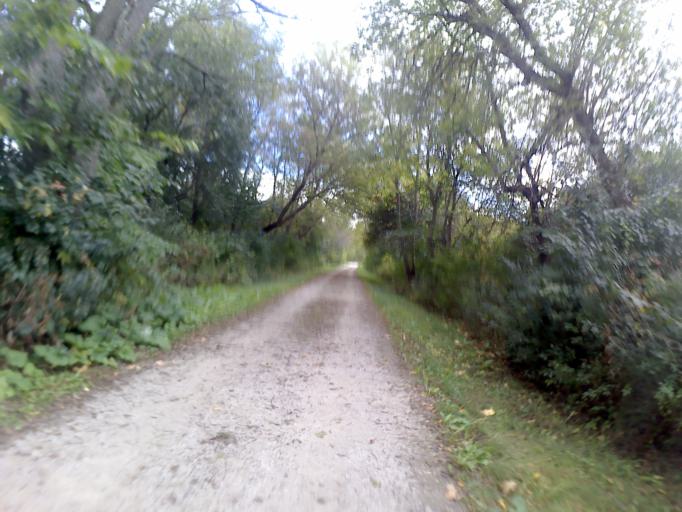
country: US
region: Illinois
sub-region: DuPage County
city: Wayne
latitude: 41.9418
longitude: -88.2315
